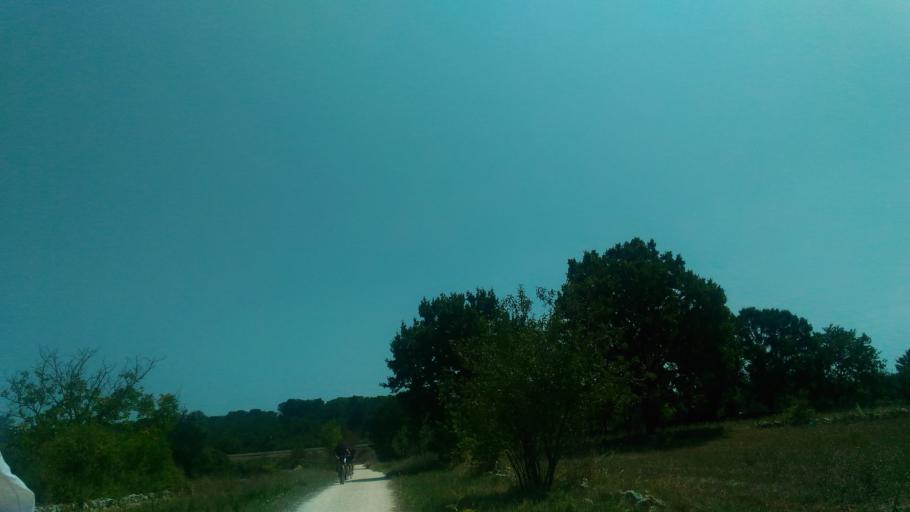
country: IT
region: Apulia
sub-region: Provincia di Brindisi
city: Cisternino
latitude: 40.7366
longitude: 17.3879
